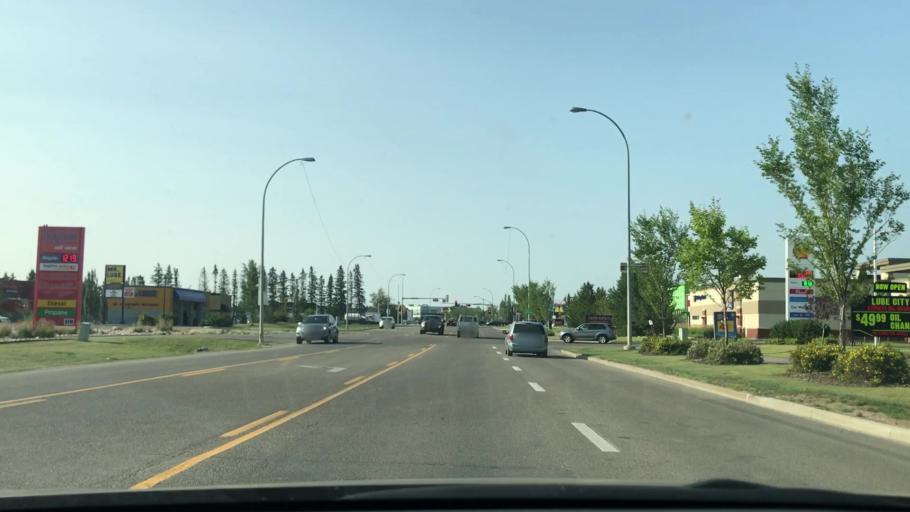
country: CA
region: Alberta
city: Beaumont
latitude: 53.4271
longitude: -113.4800
